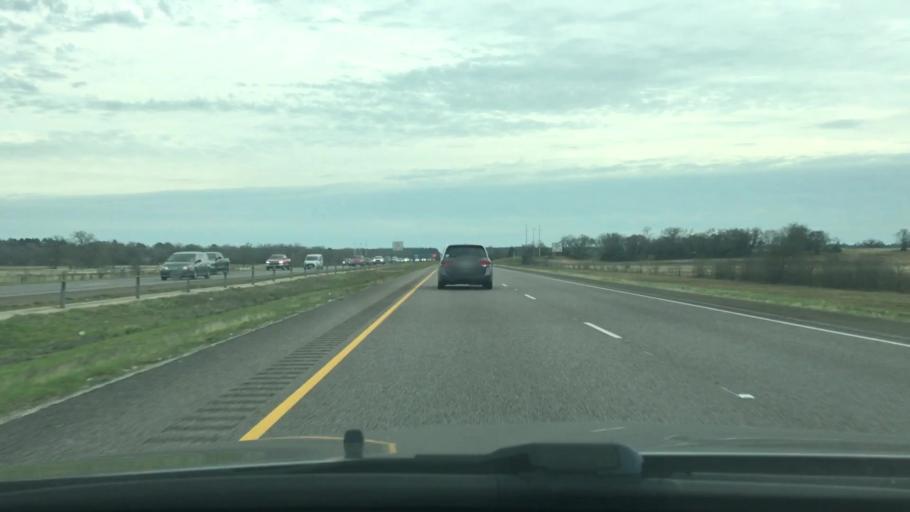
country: US
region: Texas
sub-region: Madison County
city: Madisonville
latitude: 30.9043
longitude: -95.7853
